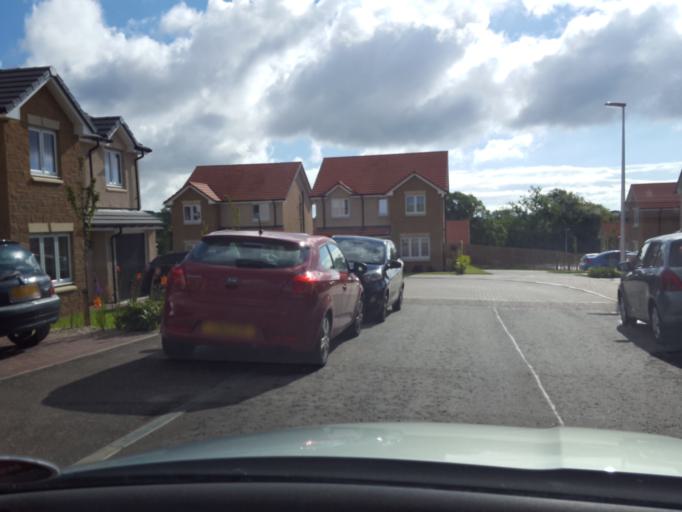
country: GB
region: Scotland
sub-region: Fife
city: Crossgates
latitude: 56.0556
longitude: -3.4007
